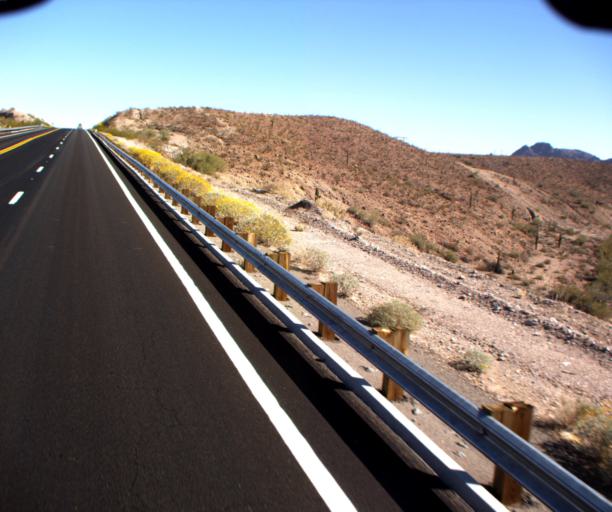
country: US
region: Arizona
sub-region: La Paz County
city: Quartzsite
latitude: 33.2393
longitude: -114.2487
